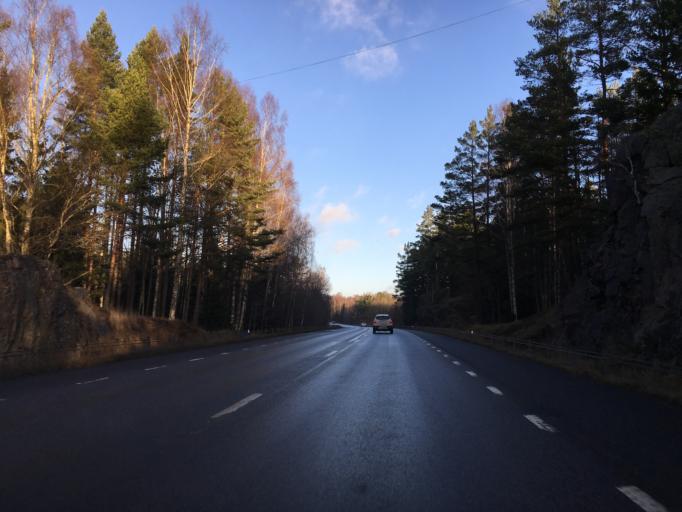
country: SE
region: Kalmar
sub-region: Vasterviks Kommun
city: Ankarsrum
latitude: 57.6759
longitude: 16.4436
